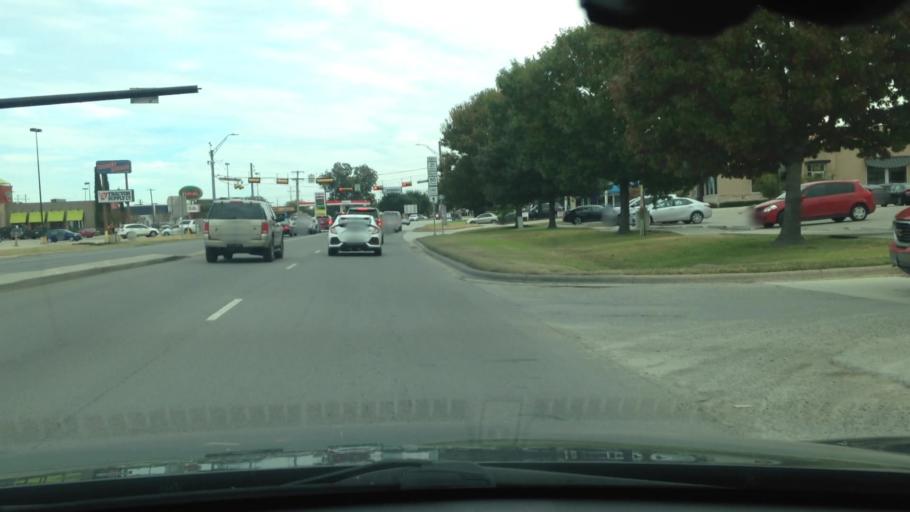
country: US
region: Texas
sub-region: Hays County
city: San Marcos
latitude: 29.8818
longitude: -97.9196
